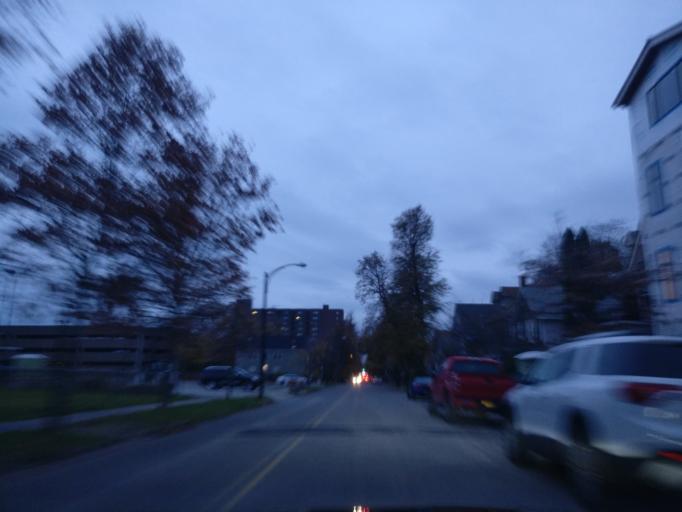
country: US
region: New York
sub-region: Erie County
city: Buffalo
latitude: 42.9113
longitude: -78.8735
